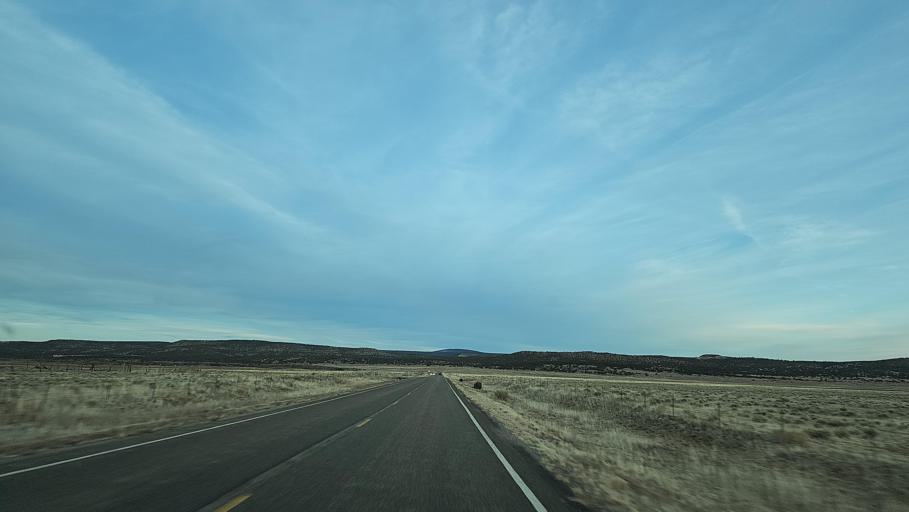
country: US
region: New Mexico
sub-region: Cibola County
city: Grants
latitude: 34.7091
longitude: -108.0037
